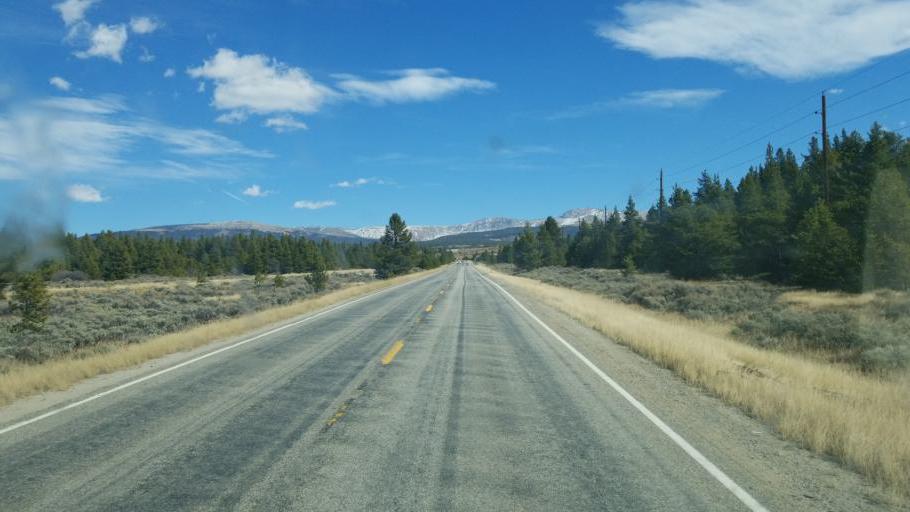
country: US
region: Colorado
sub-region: Lake County
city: Leadville North
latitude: 39.2262
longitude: -106.3389
